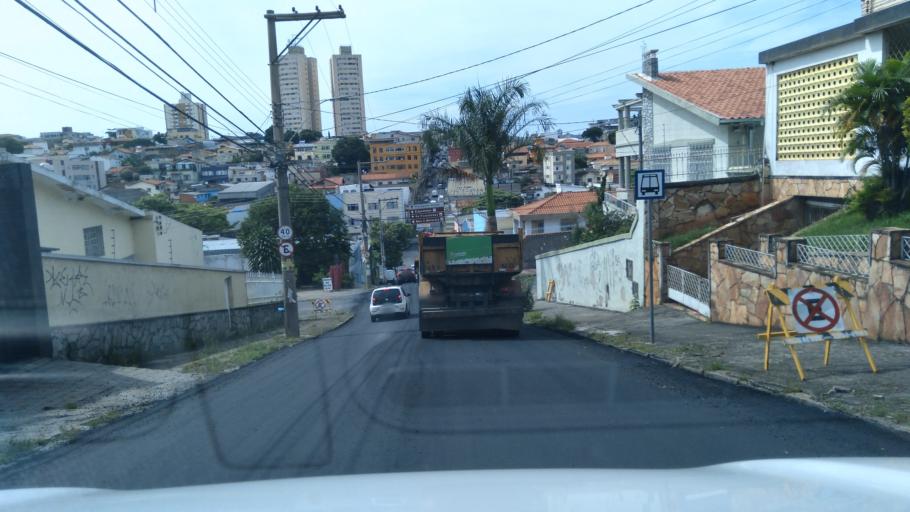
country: BR
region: Minas Gerais
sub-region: Belo Horizonte
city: Belo Horizonte
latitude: -19.9083
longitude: -43.9651
